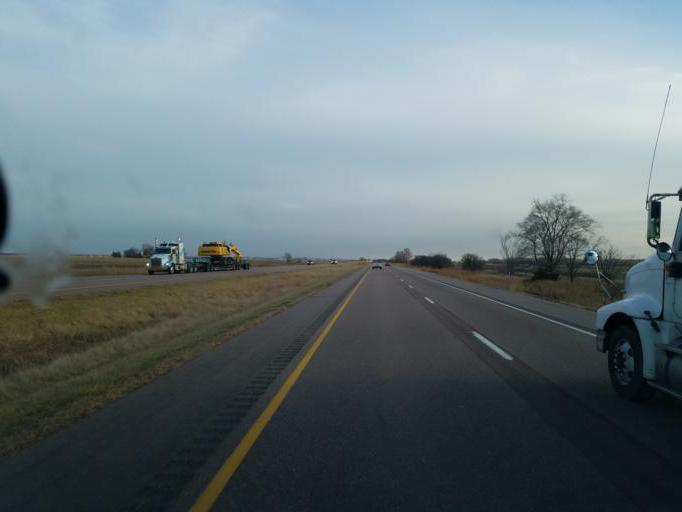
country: US
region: Iowa
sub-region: Monona County
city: Onawa
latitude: 42.0686
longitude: -96.1667
